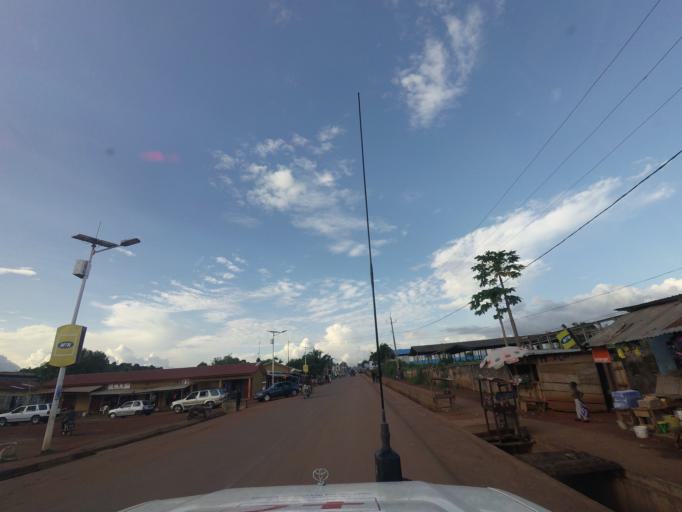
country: GN
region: Nzerekore
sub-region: Nzerekore Prefecture
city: Nzerekore
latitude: 7.7367
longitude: -8.8279
